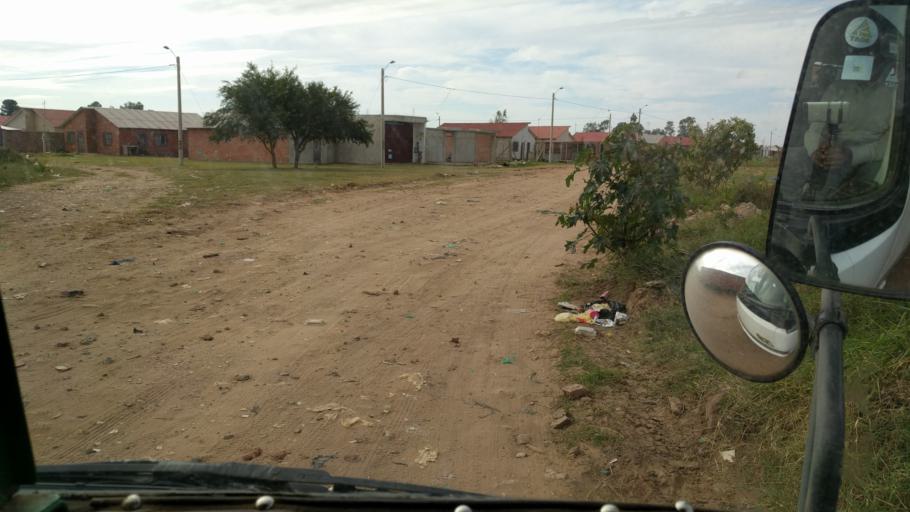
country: BO
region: Santa Cruz
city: Santa Cruz de la Sierra
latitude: -17.6866
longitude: -63.1438
